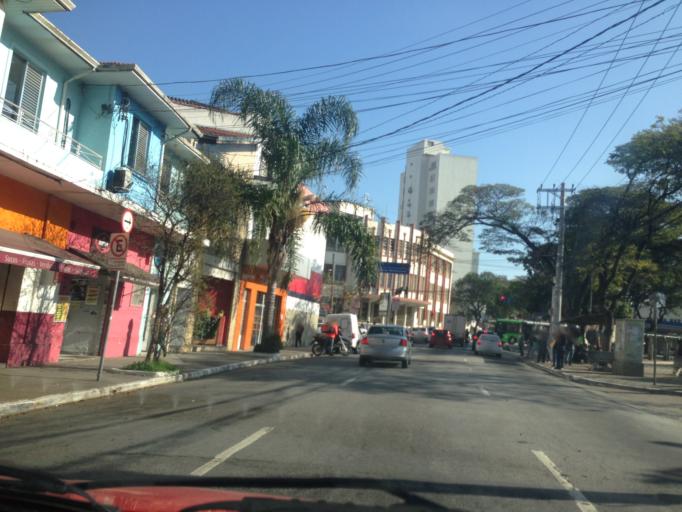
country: BR
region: Sao Paulo
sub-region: Sao Paulo
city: Sao Paulo
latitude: -23.5239
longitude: -46.7049
